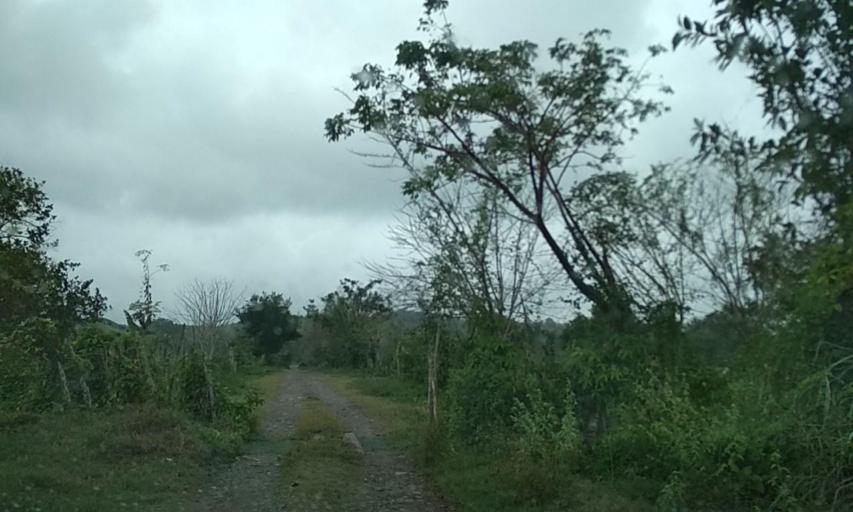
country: MX
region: Veracruz
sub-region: Papantla
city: El Chote
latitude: 20.3766
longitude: -97.3436
